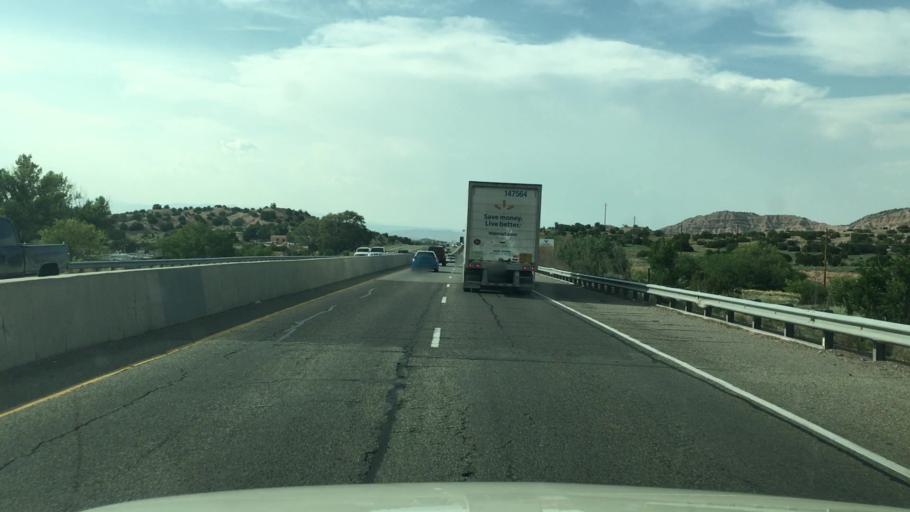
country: US
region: New Mexico
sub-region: Santa Fe County
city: Nambe
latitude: 35.8083
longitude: -105.9656
